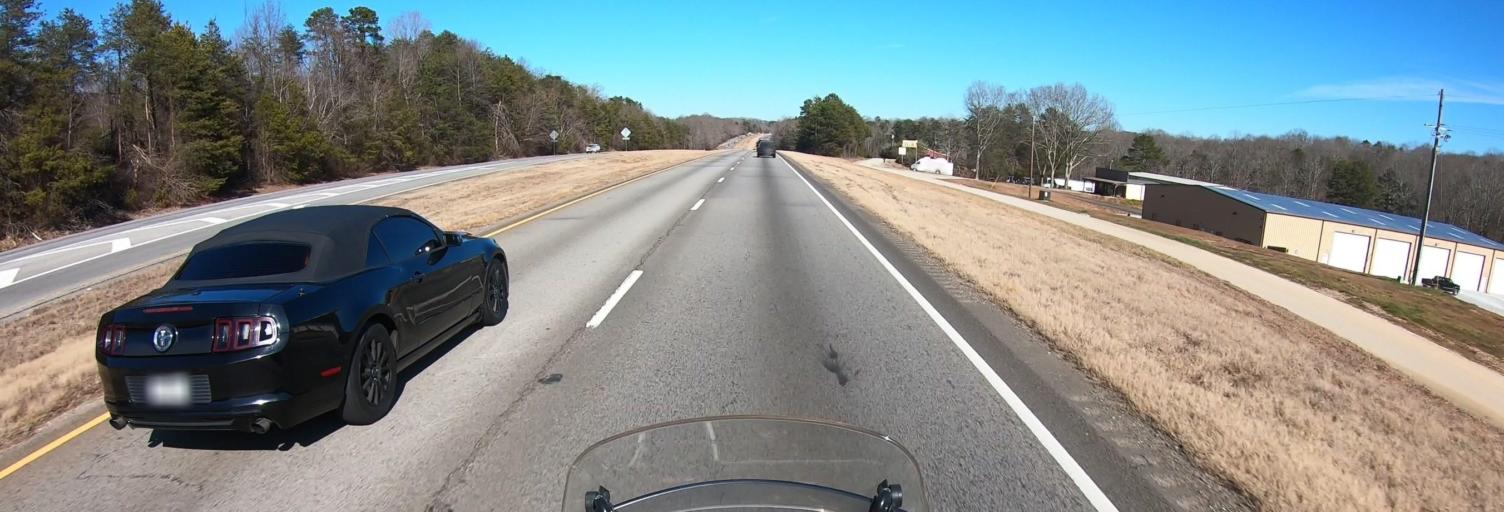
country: US
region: Georgia
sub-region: Habersham County
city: Raoul
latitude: 34.4586
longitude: -83.6075
